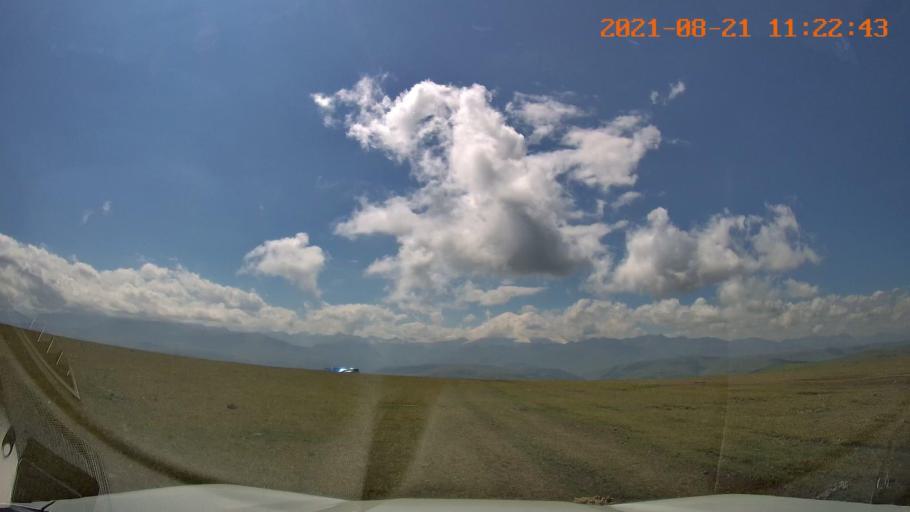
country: RU
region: Stavropol'skiy
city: Kislovodsk
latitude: 43.6144
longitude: 42.5916
